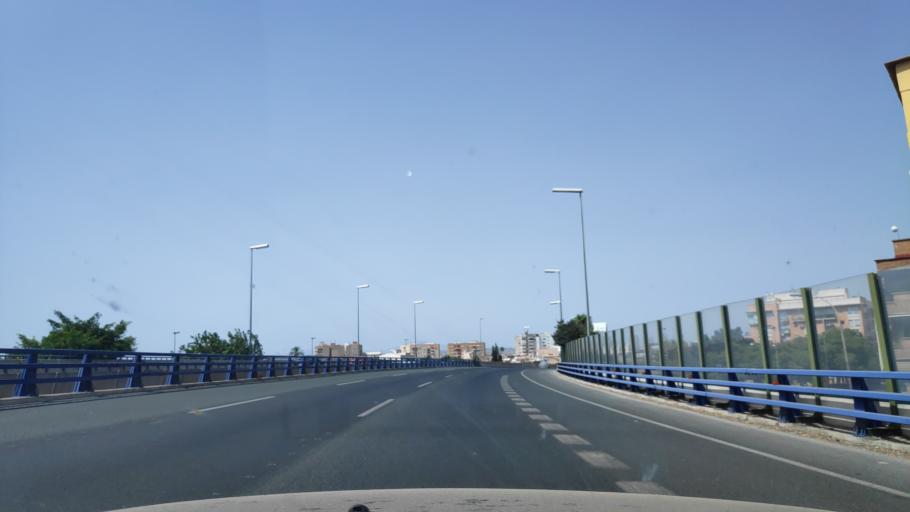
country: ES
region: Murcia
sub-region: Murcia
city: Murcia
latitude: 37.9699
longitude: -1.1382
